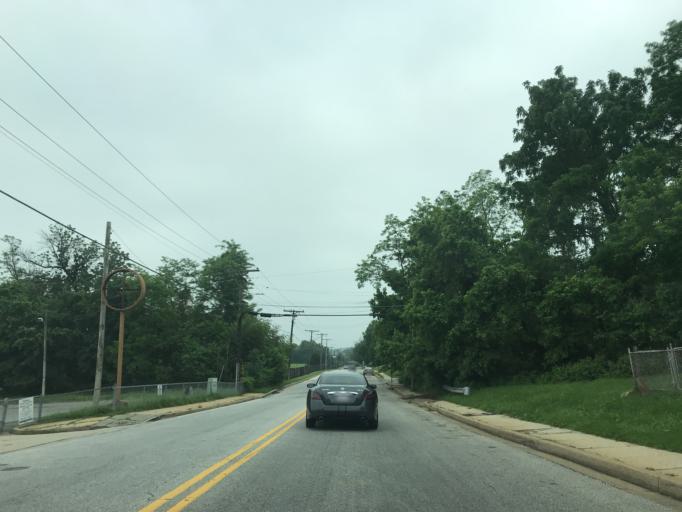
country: US
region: Maryland
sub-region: Baltimore County
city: Charlestown
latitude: 39.2724
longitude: -76.6929
